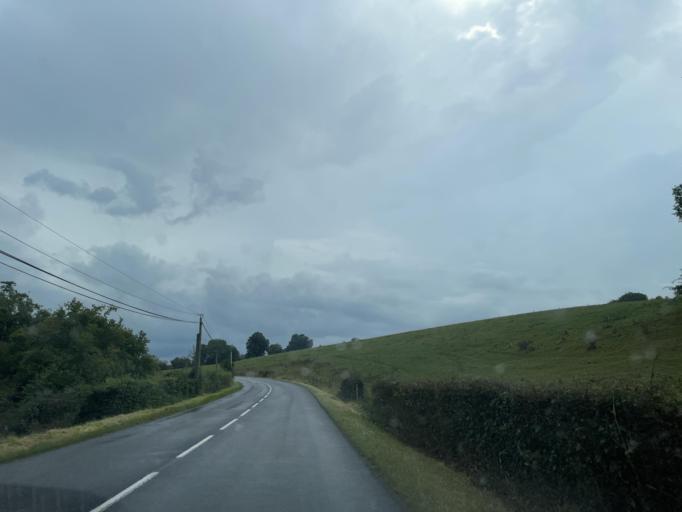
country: FR
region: Haute-Normandie
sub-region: Departement de la Seine-Maritime
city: Neufchatel-en-Bray
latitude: 49.7180
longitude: 1.4323
